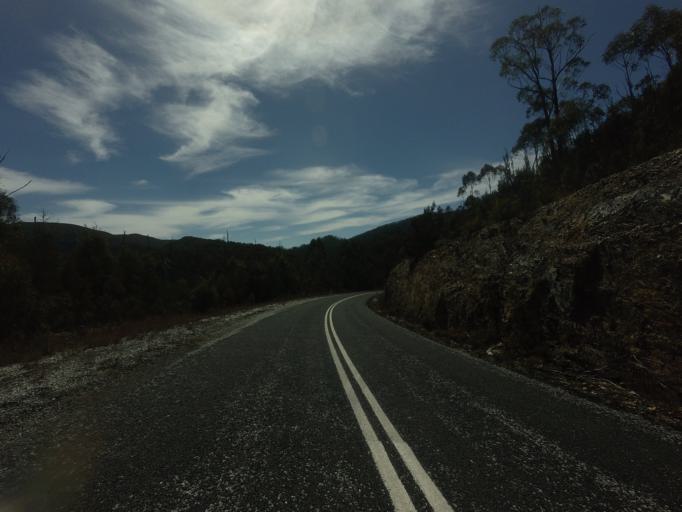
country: AU
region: Tasmania
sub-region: West Coast
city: Queenstown
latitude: -42.8047
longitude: 146.0952
